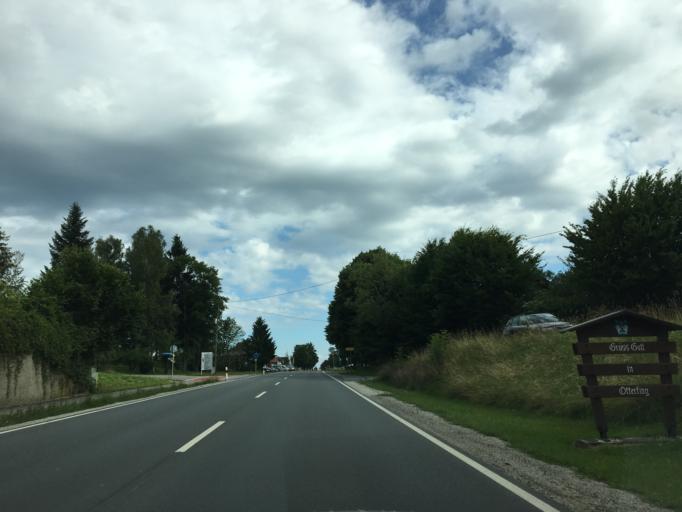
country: DE
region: Bavaria
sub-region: Upper Bavaria
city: Otterfing
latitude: 47.8964
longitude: 11.6772
